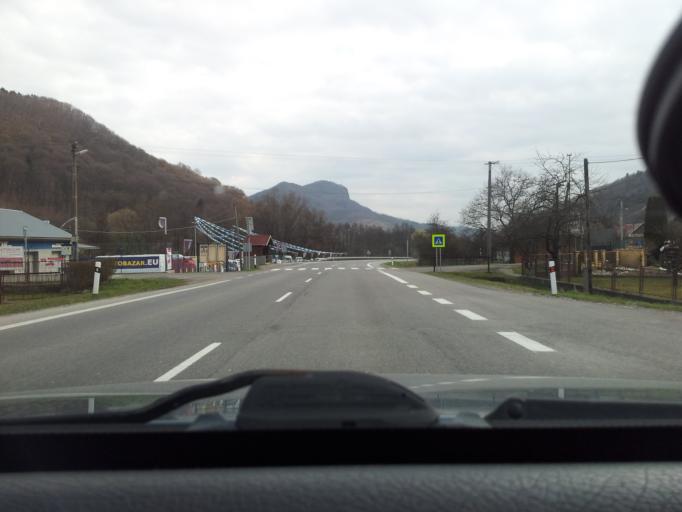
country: SK
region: Banskobystricky
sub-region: Okres Ziar nad Hronom
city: Kremnica
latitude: 48.6644
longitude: 18.9114
